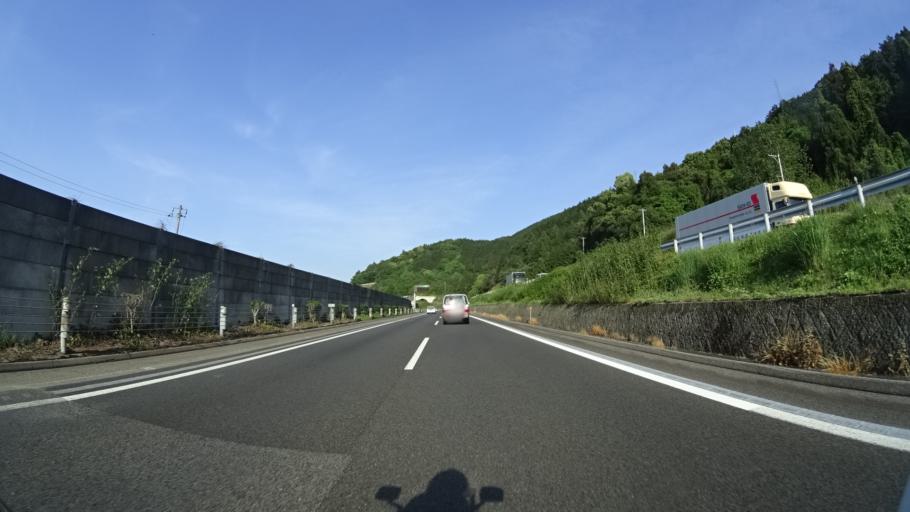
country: JP
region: Ehime
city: Kawanoecho
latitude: 33.9645
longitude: 133.5335
